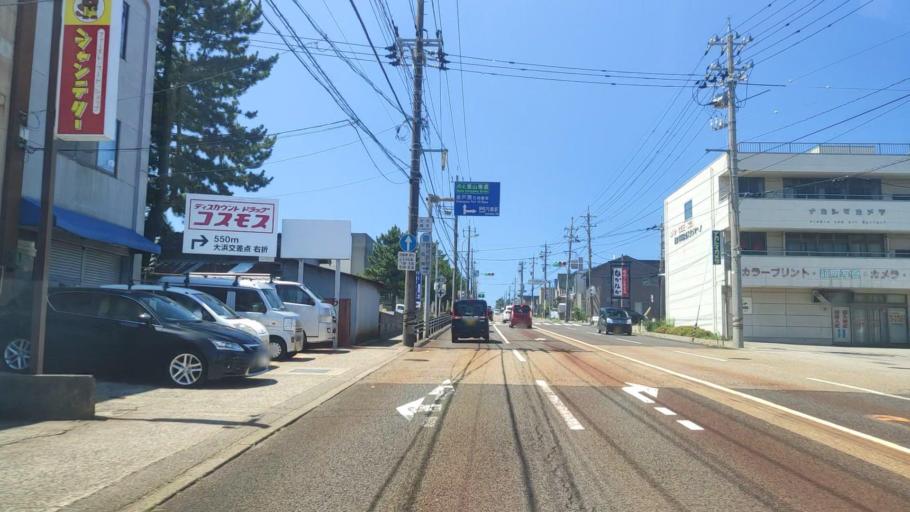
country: JP
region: Ishikawa
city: Kanazawa-shi
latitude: 36.6232
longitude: 136.6251
